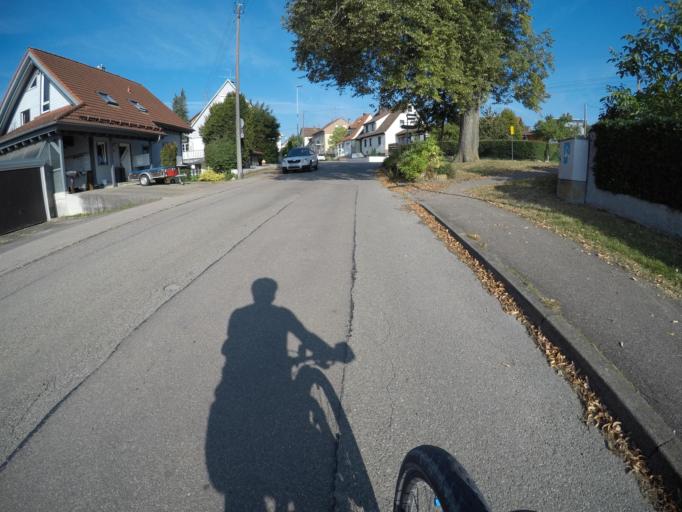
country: DE
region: Baden-Wuerttemberg
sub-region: Regierungsbezirk Stuttgart
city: Gerstetten
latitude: 48.6189
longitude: 10.0293
